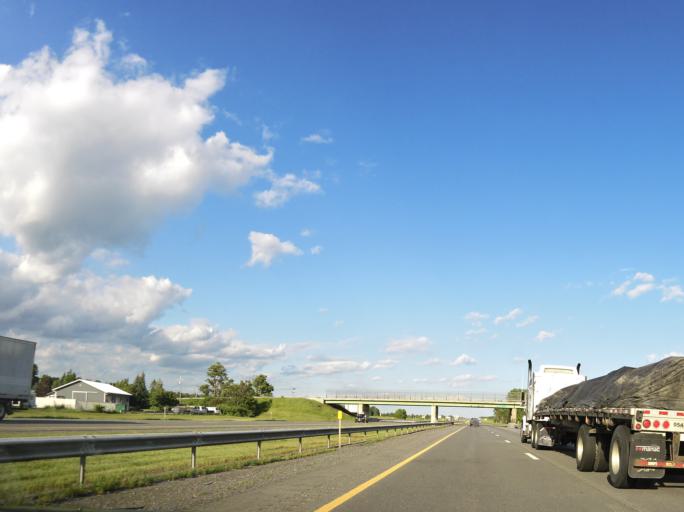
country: US
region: New York
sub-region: Genesee County
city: Batavia
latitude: 43.0191
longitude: -78.1802
